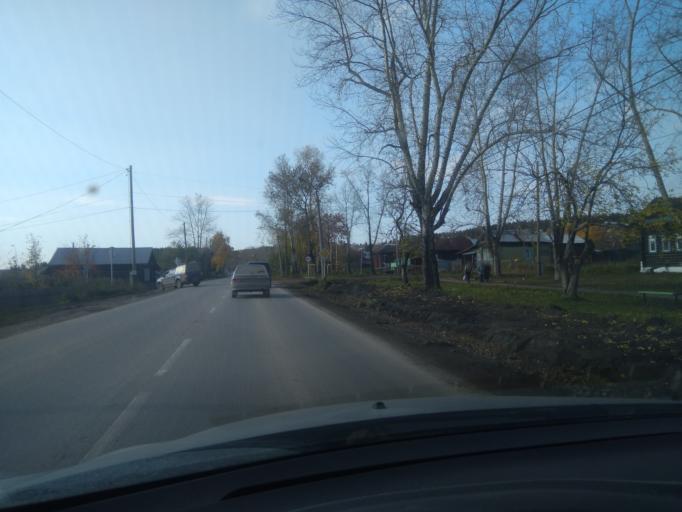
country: RU
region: Sverdlovsk
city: Nizhniye Sergi
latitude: 56.6567
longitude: 59.2976
